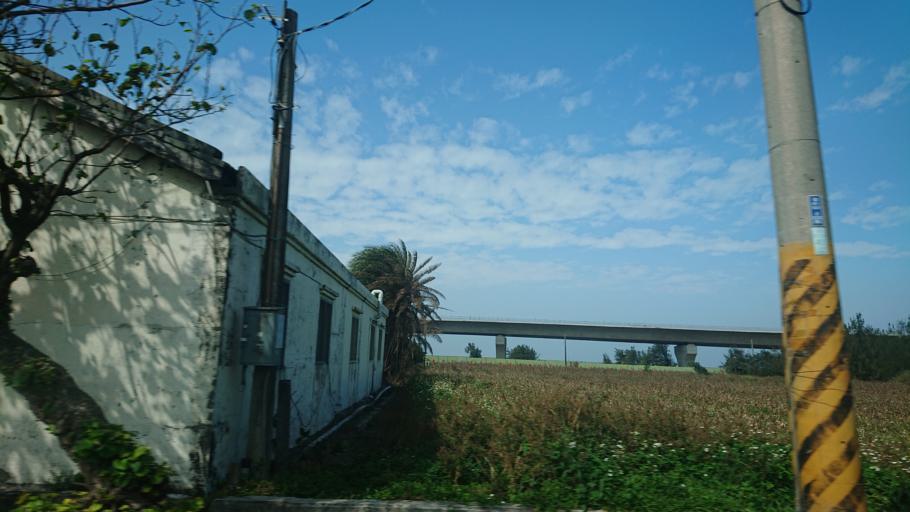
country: TW
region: Taiwan
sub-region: Changhua
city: Chang-hua
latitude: 23.9162
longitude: 120.3122
